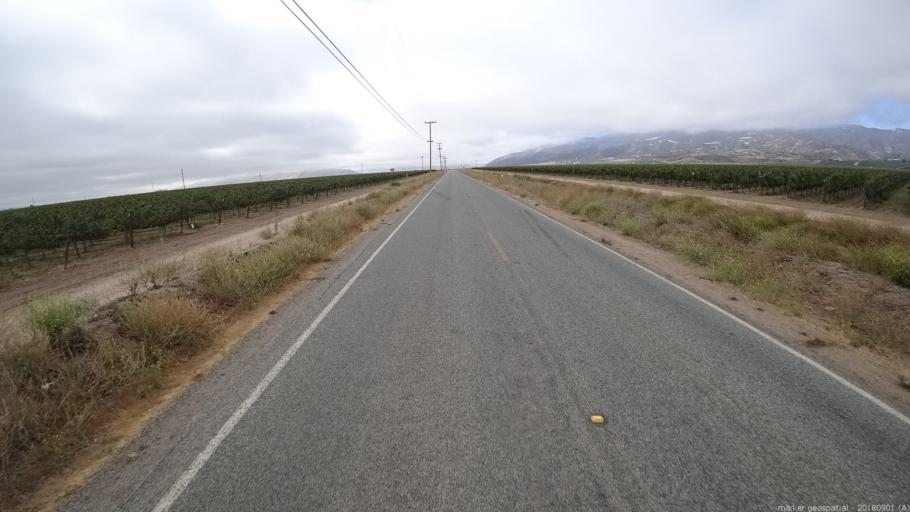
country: US
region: California
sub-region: Monterey County
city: Soledad
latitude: 36.3525
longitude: -121.3205
